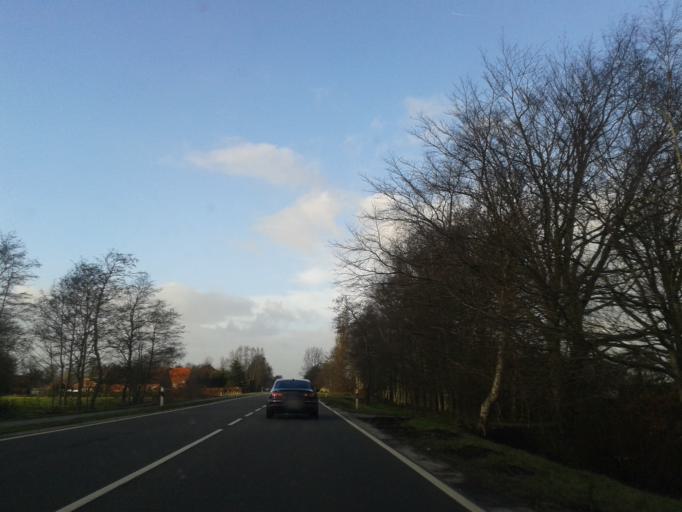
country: DE
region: Lower Saxony
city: Osteel
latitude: 53.5410
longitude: 7.2604
